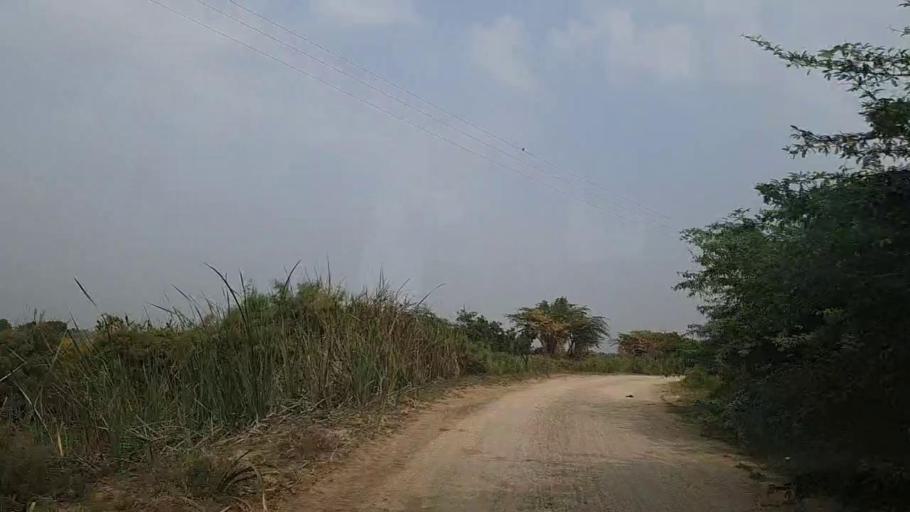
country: PK
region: Sindh
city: Mirpur Sakro
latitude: 24.6145
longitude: 67.7201
